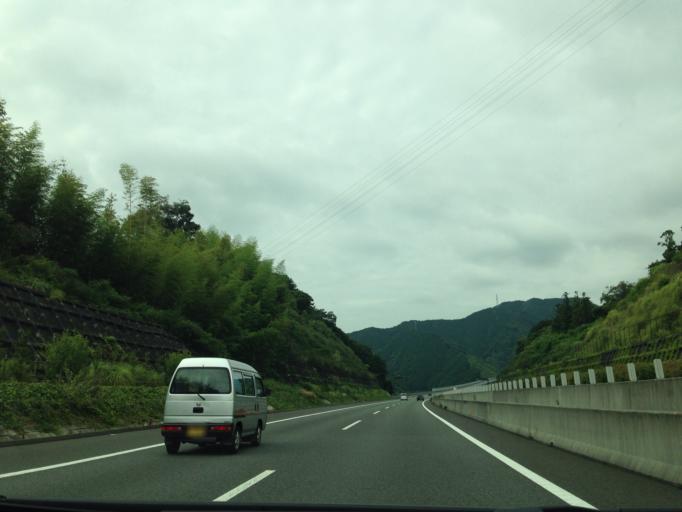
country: JP
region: Shizuoka
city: Shizuoka-shi
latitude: 35.0256
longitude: 138.3546
